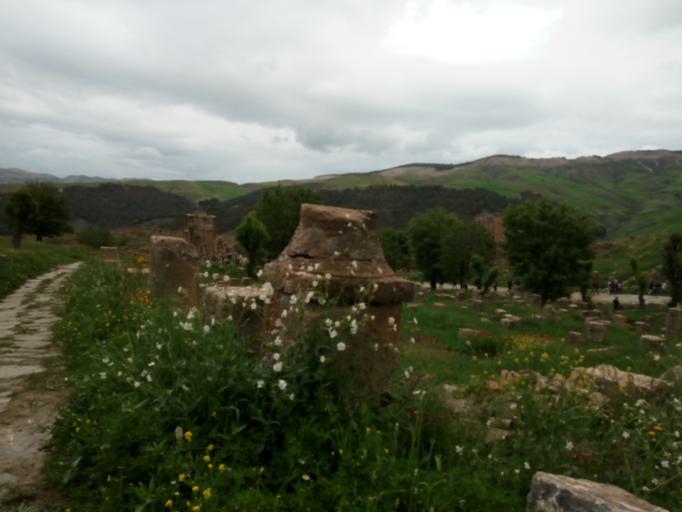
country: DZ
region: Setif
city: El Eulma
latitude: 36.3193
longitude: 5.7357
